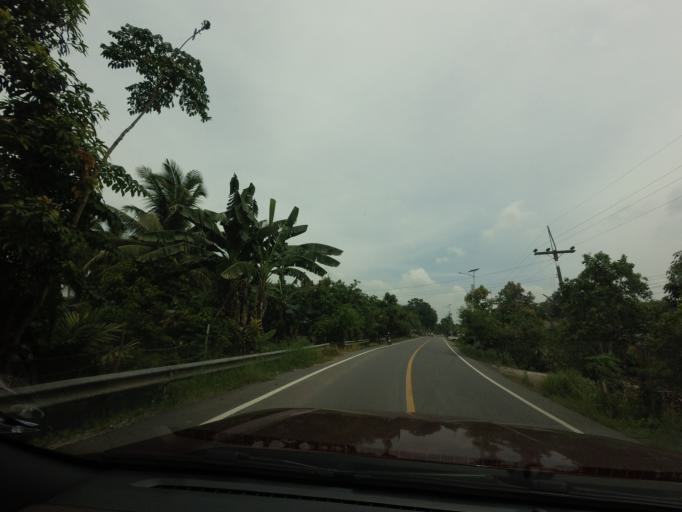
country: TH
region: Pattani
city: Yarang
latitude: 6.7133
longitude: 101.3064
